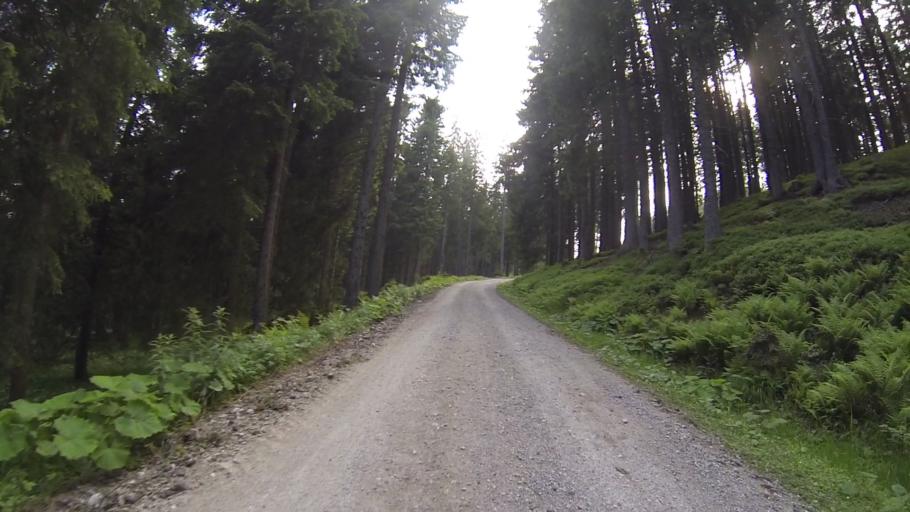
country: DE
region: Bavaria
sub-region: Swabia
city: Nesselwang
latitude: 47.5911
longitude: 10.5076
